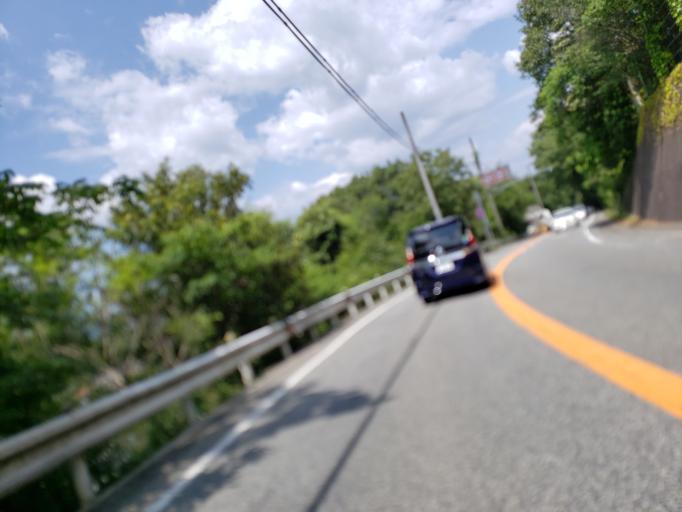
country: JP
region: Hyogo
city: Aioi
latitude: 34.7994
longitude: 134.4499
